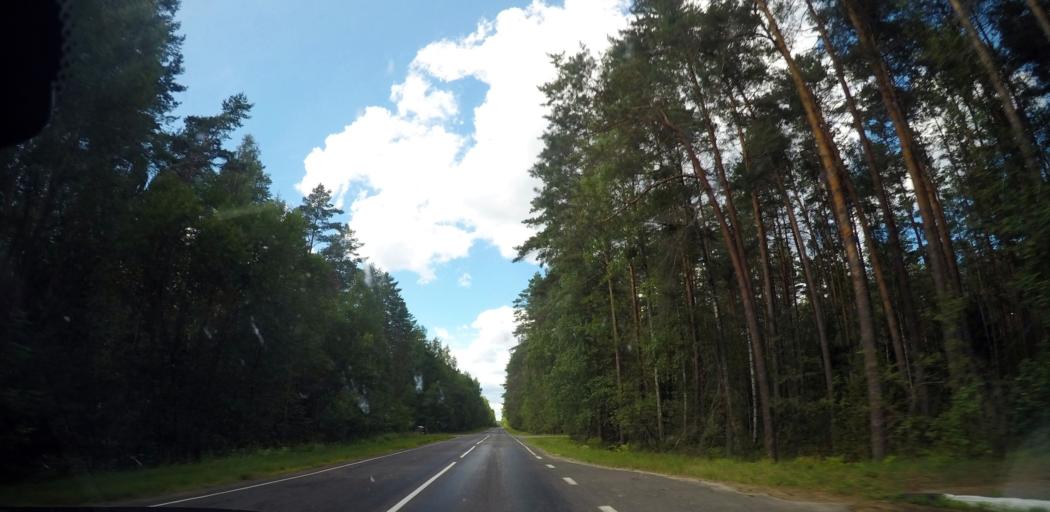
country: BY
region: Grodnenskaya
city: Skidal'
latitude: 53.8429
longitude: 24.2111
